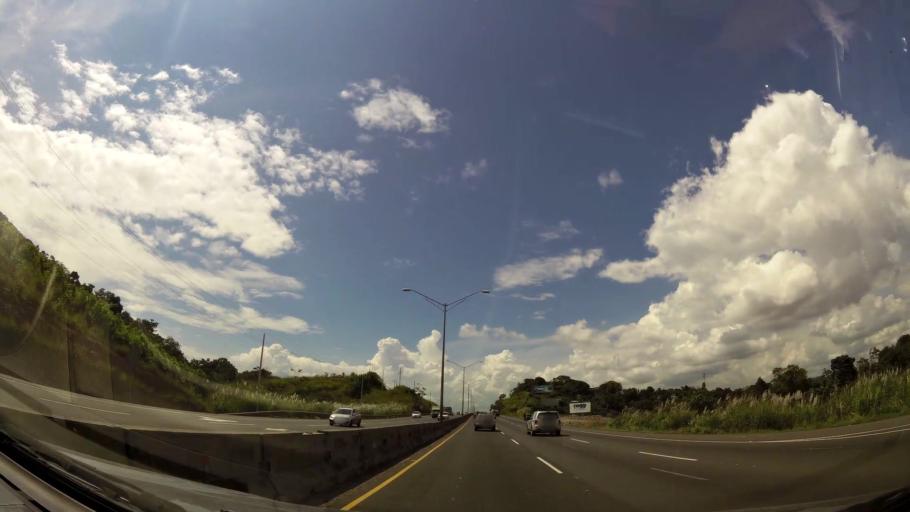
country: PA
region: Panama
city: Vista Alegre
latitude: 8.9306
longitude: -79.6875
